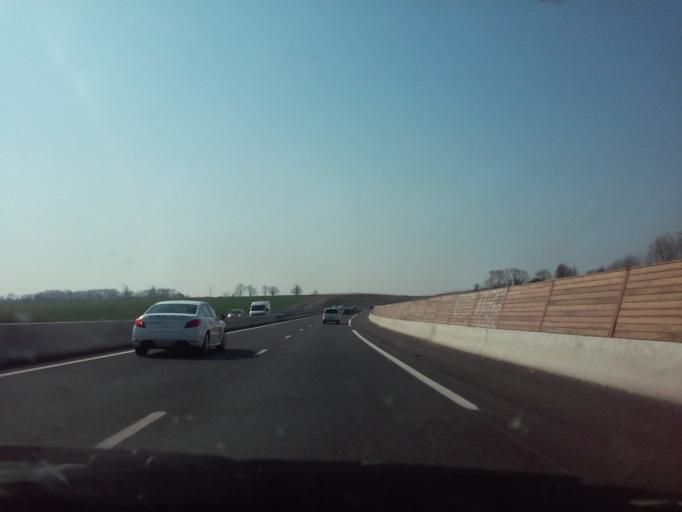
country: FR
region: Lower Normandy
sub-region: Departement du Calvados
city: Creully
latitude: 49.2252
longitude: -0.5628
